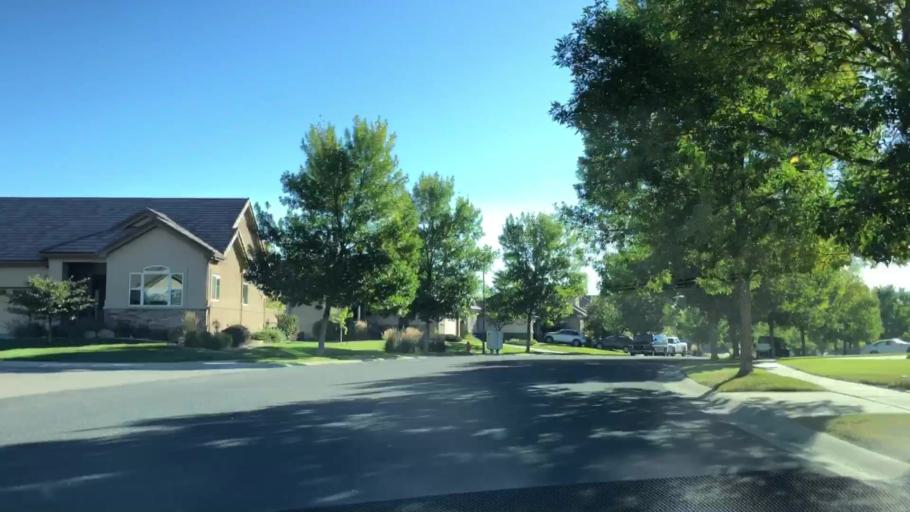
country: US
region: Colorado
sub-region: Larimer County
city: Loveland
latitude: 40.3962
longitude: -105.1406
